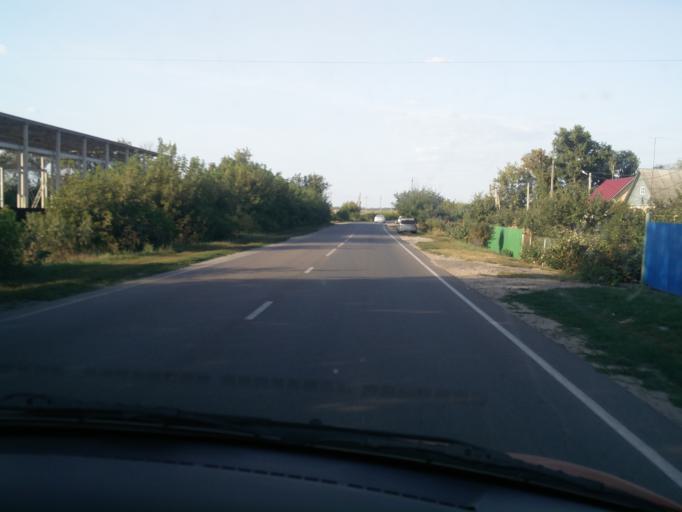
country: RU
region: Voronezj
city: Ramon'
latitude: 51.9229
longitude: 39.3229
